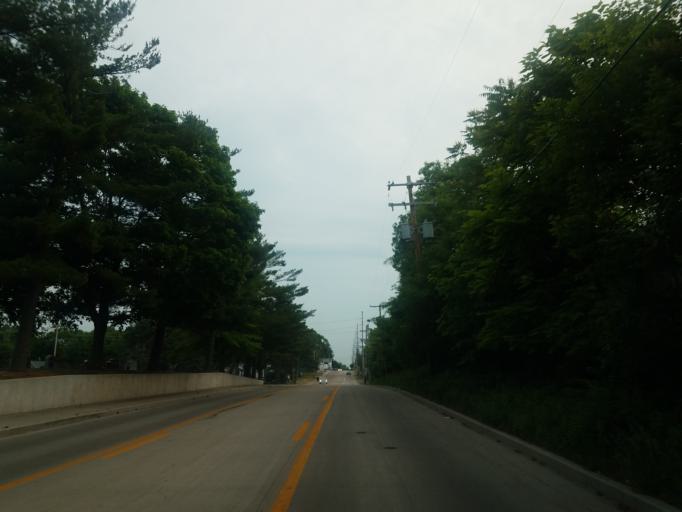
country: US
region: Illinois
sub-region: McLean County
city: Bloomington
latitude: 40.4685
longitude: -89.0063
